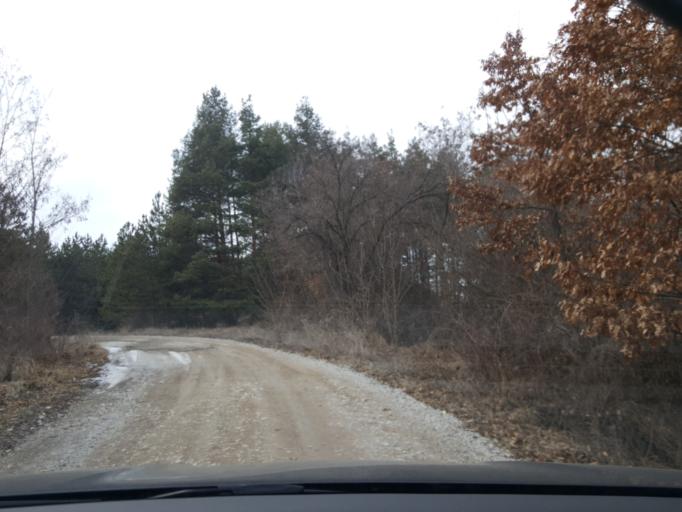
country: RS
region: Central Serbia
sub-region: Pirotski Okrug
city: Dimitrovgrad
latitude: 43.0049
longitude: 22.7469
